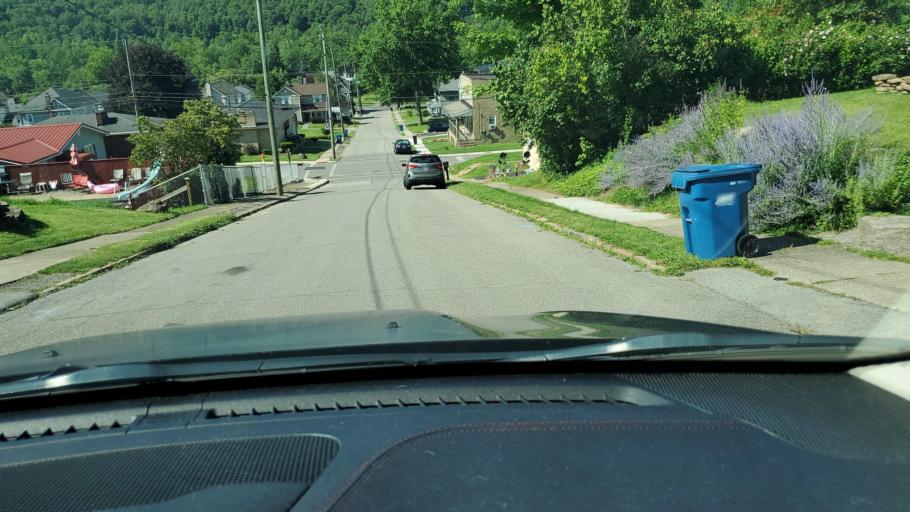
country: US
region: Ohio
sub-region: Mahoning County
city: Lowellville
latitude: 41.0419
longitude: -80.5385
